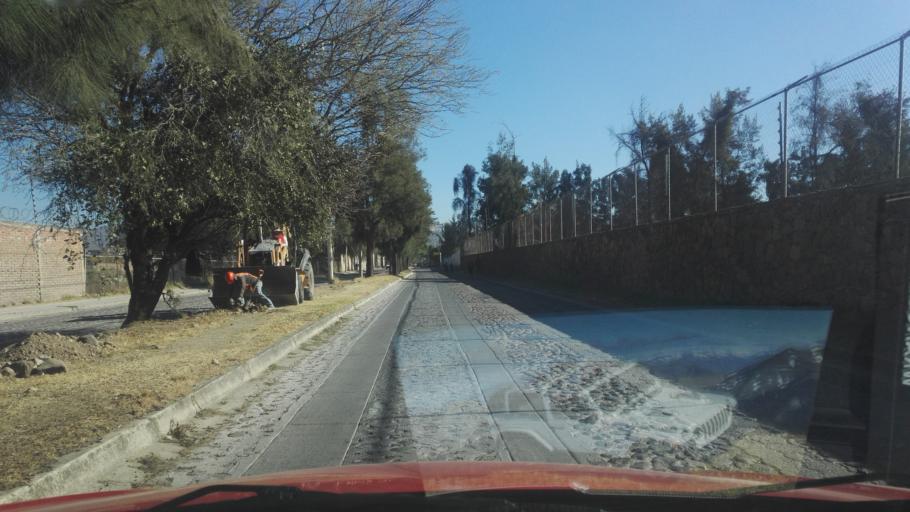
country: MX
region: Guanajuato
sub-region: Leon
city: Fraccionamiento Paraiso Real
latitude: 21.0916
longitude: -101.6082
